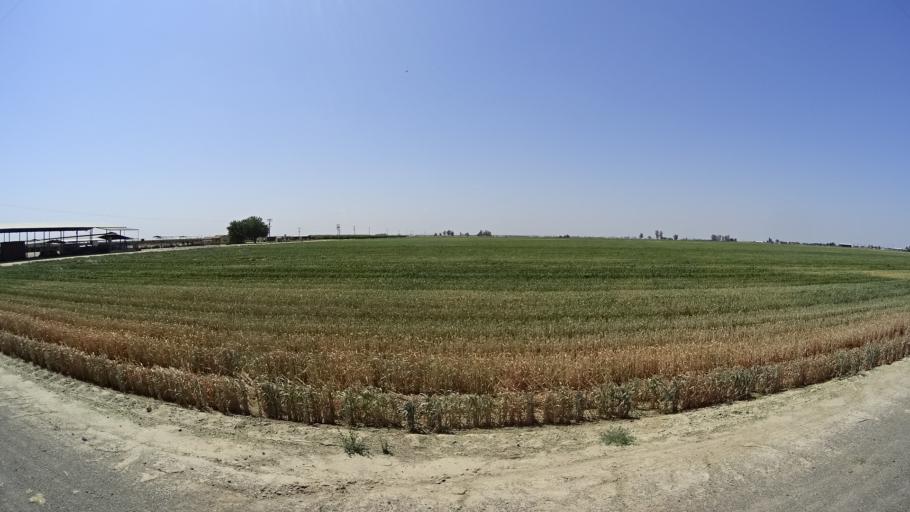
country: US
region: California
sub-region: Kings County
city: Home Garden
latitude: 36.2838
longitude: -119.6065
